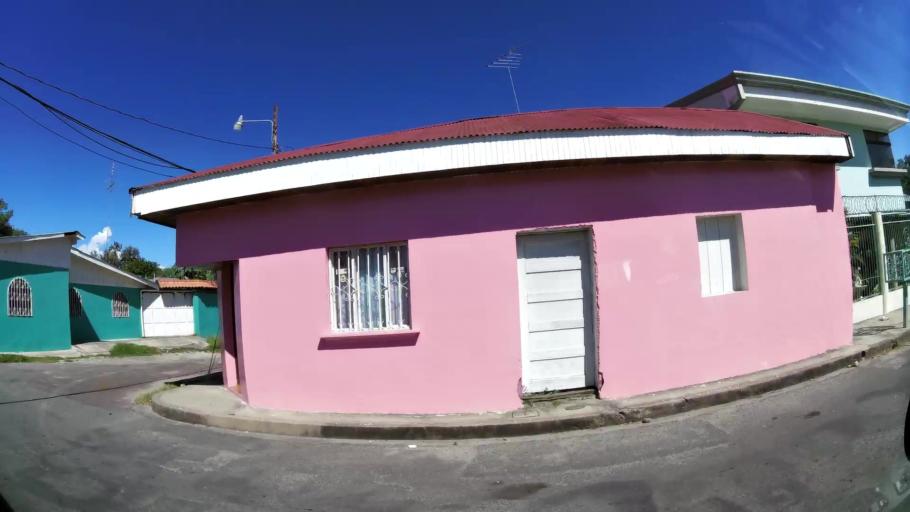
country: CR
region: Guanacaste
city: Liberia
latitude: 10.6308
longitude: -85.4334
